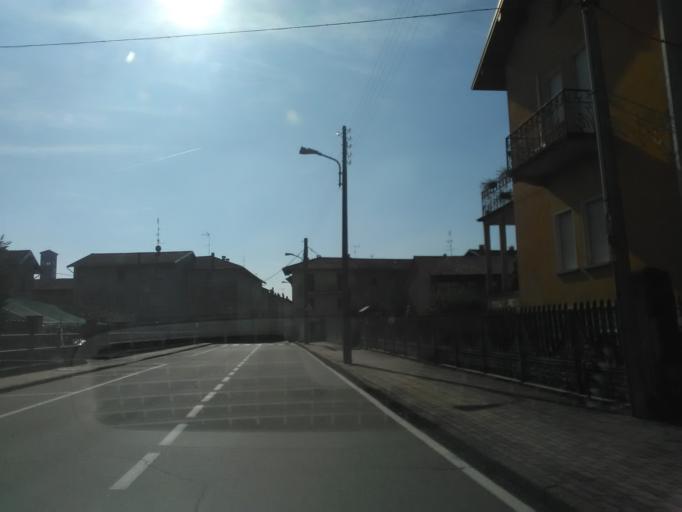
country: IT
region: Piedmont
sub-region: Provincia di Vercelli
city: Lenta
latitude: 45.5579
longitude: 8.3843
